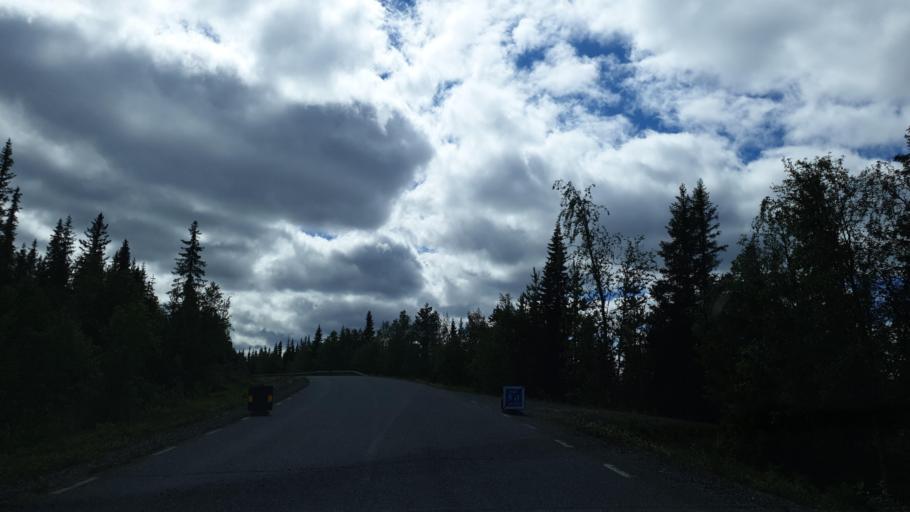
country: SE
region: Vaesterbotten
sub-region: Vilhelmina Kommun
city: Sjoberg
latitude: 65.1533
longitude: 15.8611
